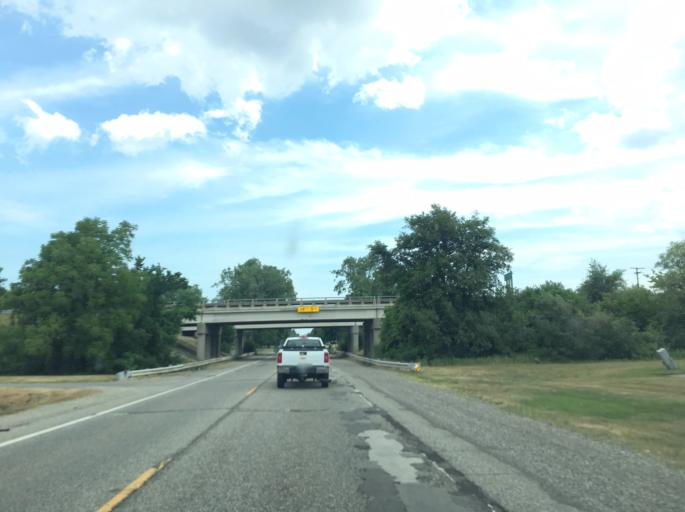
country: US
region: Michigan
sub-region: Macomb County
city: Sterling Heights
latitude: 42.6033
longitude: -83.0240
